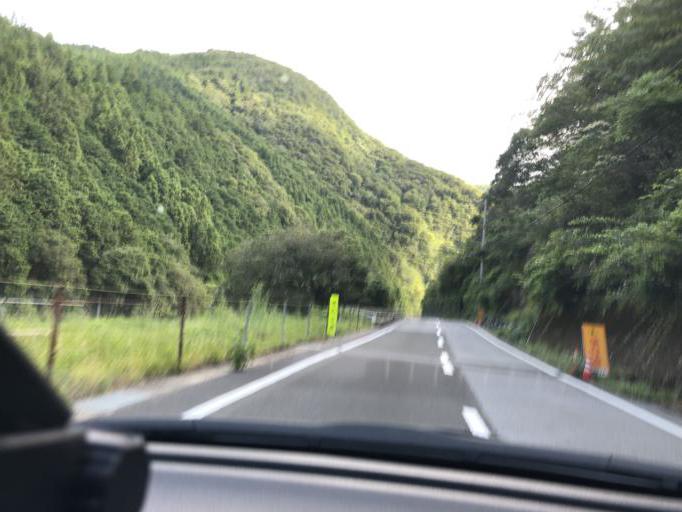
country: JP
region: Kochi
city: Kochi-shi
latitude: 33.6338
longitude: 133.5195
